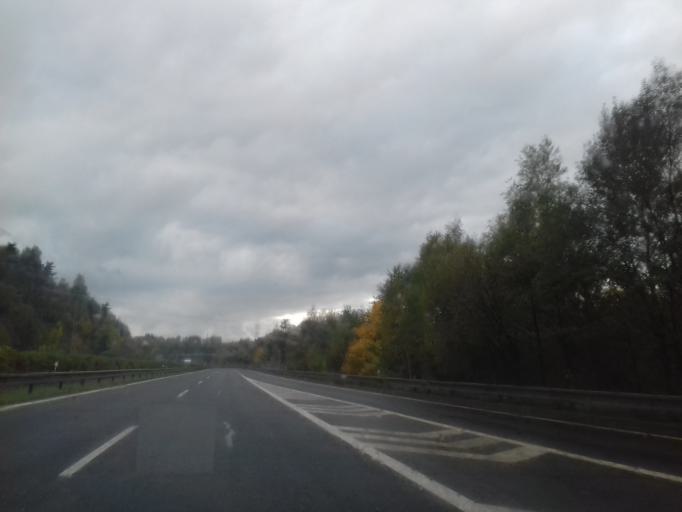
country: CZ
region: Liberecky
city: Hodkovice nad Mohelkou
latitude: 50.6663
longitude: 15.0963
